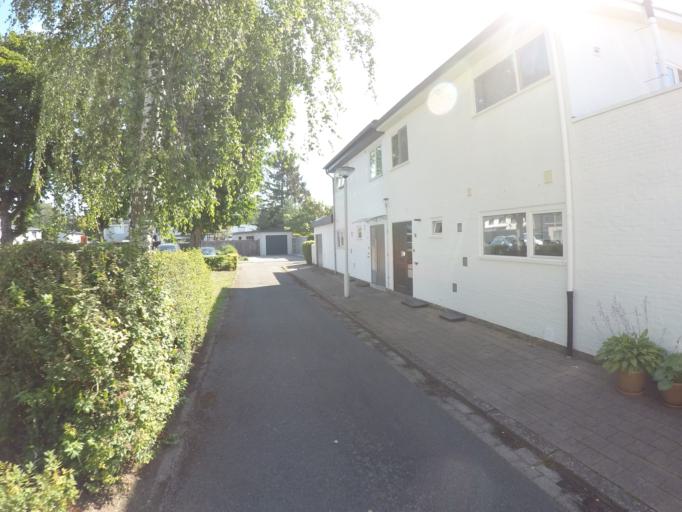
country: BE
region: Flanders
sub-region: Provincie Antwerpen
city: Kapellen
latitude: 51.3032
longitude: 4.4276
